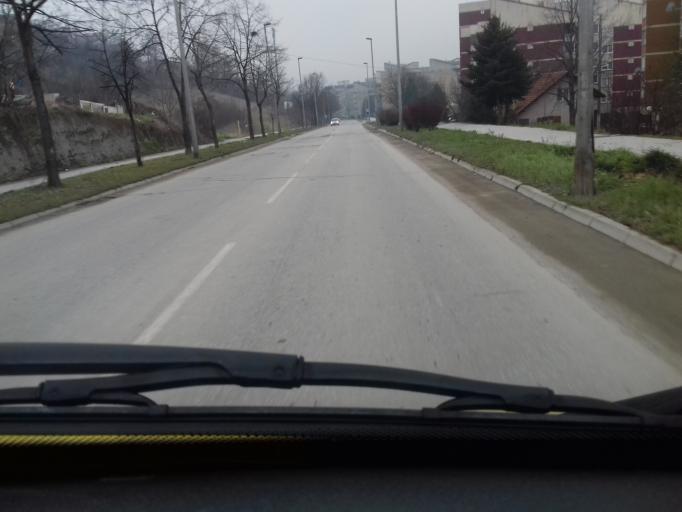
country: BA
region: Federation of Bosnia and Herzegovina
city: Zenica
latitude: 44.2030
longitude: 17.9270
